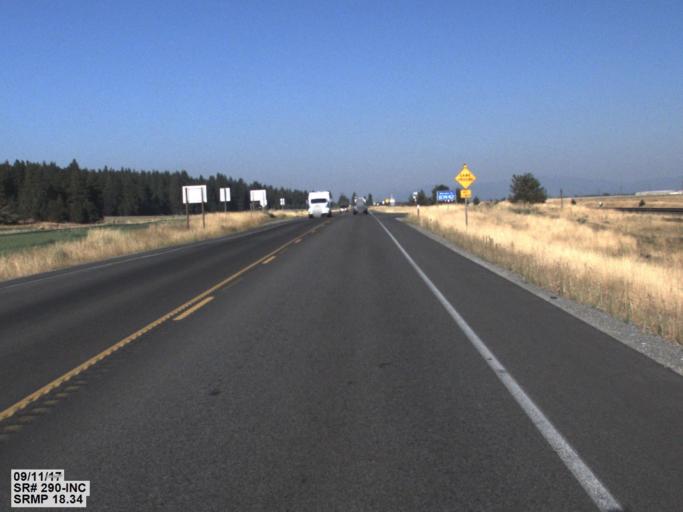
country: US
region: Washington
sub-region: Spokane County
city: Otis Orchards-East Farms
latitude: 47.7355
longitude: -117.0427
